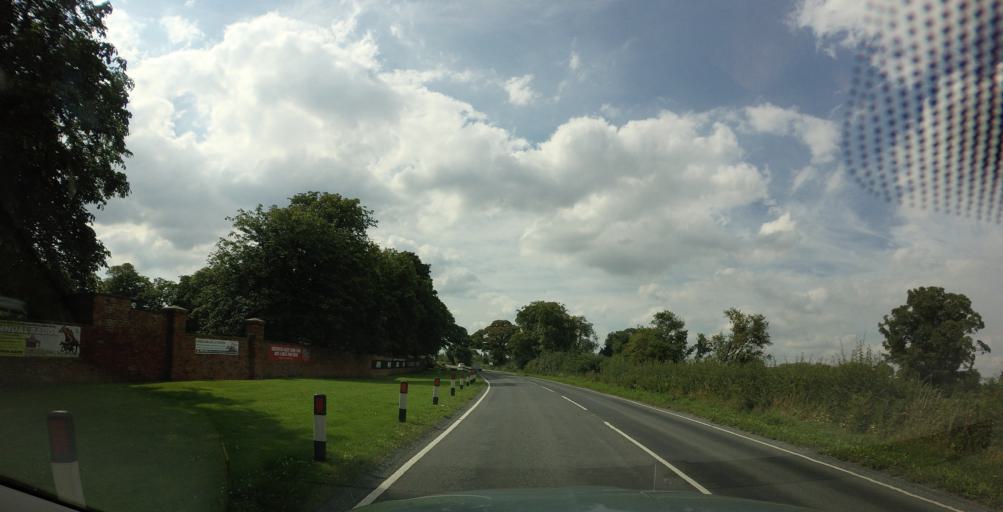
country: GB
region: England
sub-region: North Yorkshire
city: Ripon
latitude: 54.1275
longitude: -1.4984
